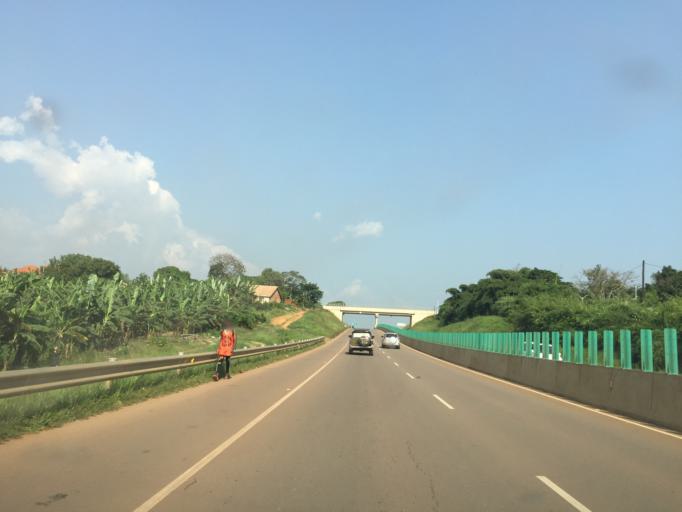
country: UG
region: Central Region
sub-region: Kampala District
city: Kampala
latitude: 0.2380
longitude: 32.6155
